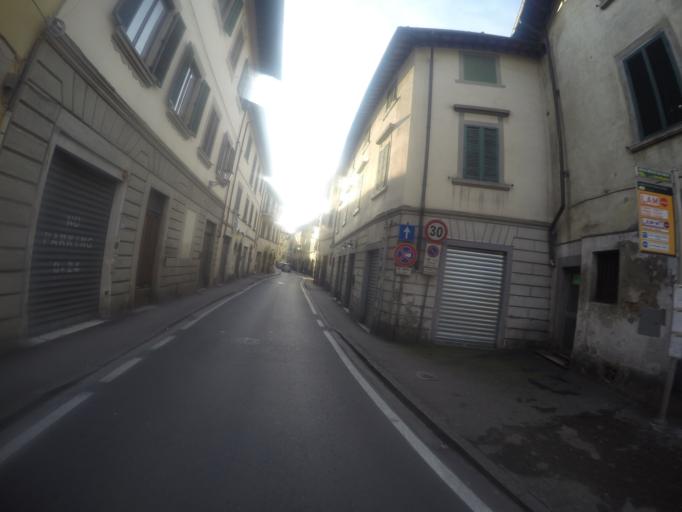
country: IT
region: Tuscany
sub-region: Provincia di Prato
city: Prato
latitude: 43.8827
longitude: 11.0989
